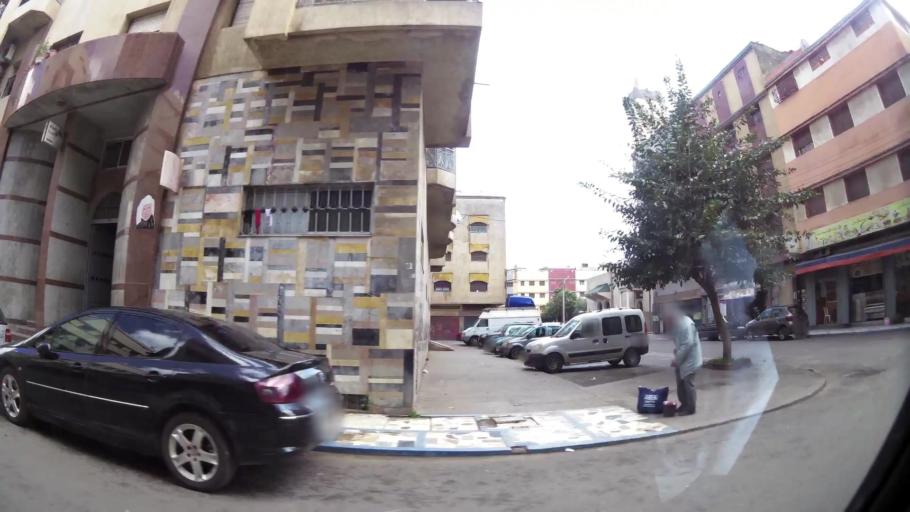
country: MA
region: Grand Casablanca
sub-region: Casablanca
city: Casablanca
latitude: 33.5364
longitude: -7.5730
